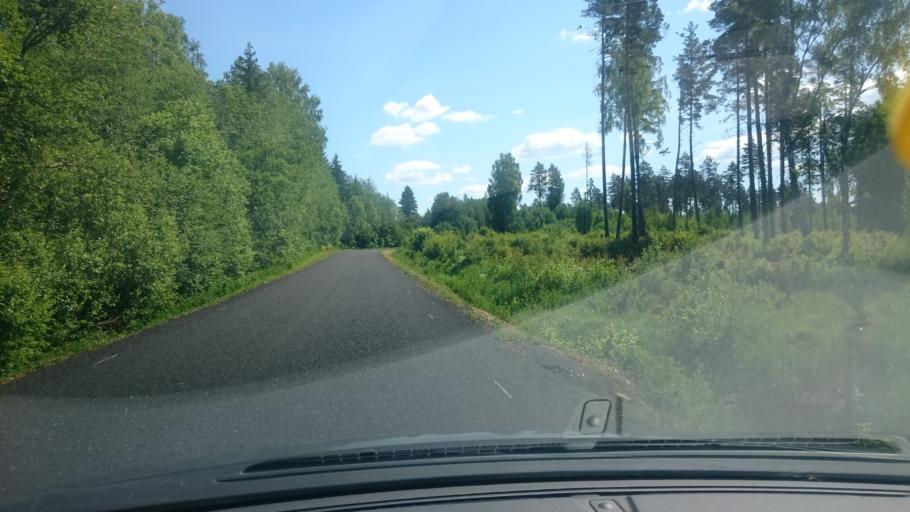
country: EE
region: Harju
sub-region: Rae vald
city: Vaida
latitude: 59.2288
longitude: 24.9938
